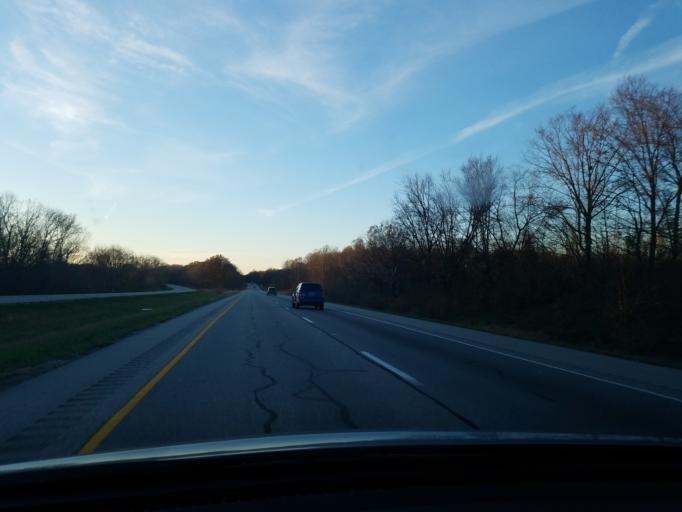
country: US
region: Indiana
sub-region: Posey County
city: Poseyville
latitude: 38.1910
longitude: -87.8351
